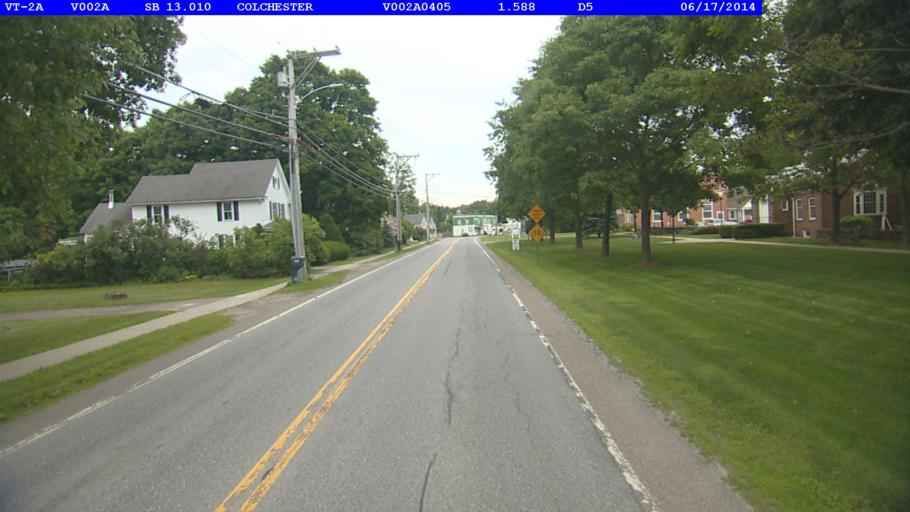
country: US
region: Vermont
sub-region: Chittenden County
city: Colchester
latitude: 44.5445
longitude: -73.1501
